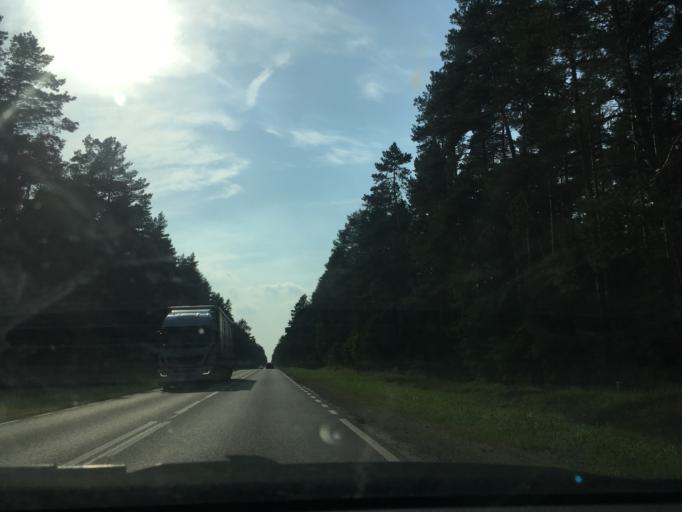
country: PL
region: Podlasie
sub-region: Powiat bialostocki
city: Suprasl
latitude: 53.1256
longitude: 23.3318
